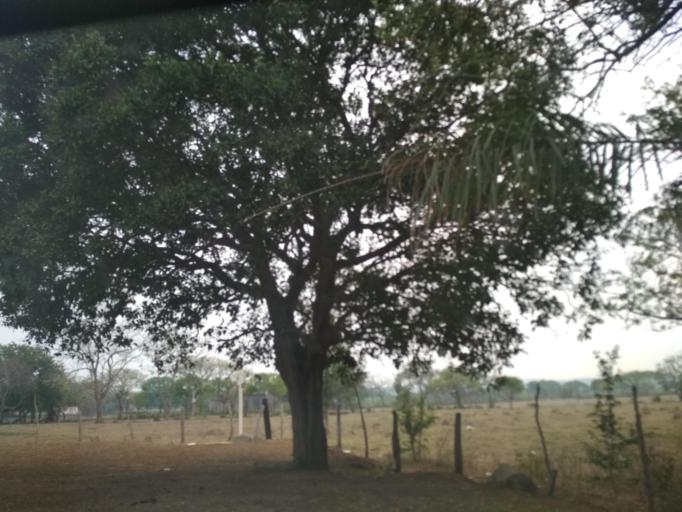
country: MX
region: Veracruz
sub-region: Veracruz
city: Fraccionamiento Geovillas los Pinos
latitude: 19.2101
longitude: -96.2462
